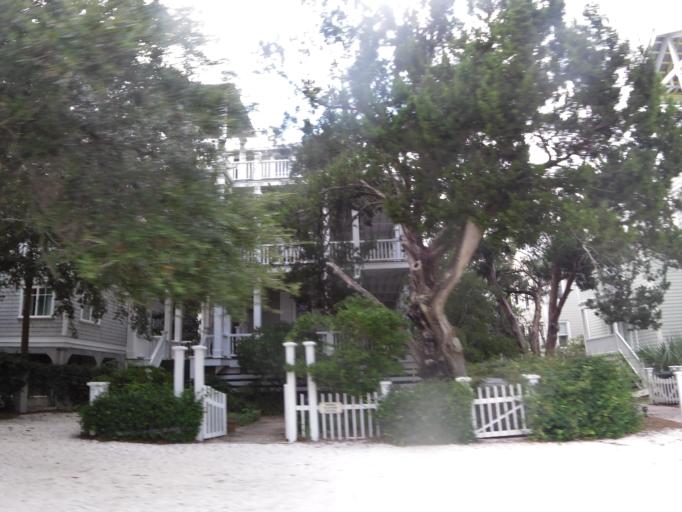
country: US
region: Georgia
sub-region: Glynn County
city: Saint Simons Island
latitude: 31.1455
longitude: -81.3744
